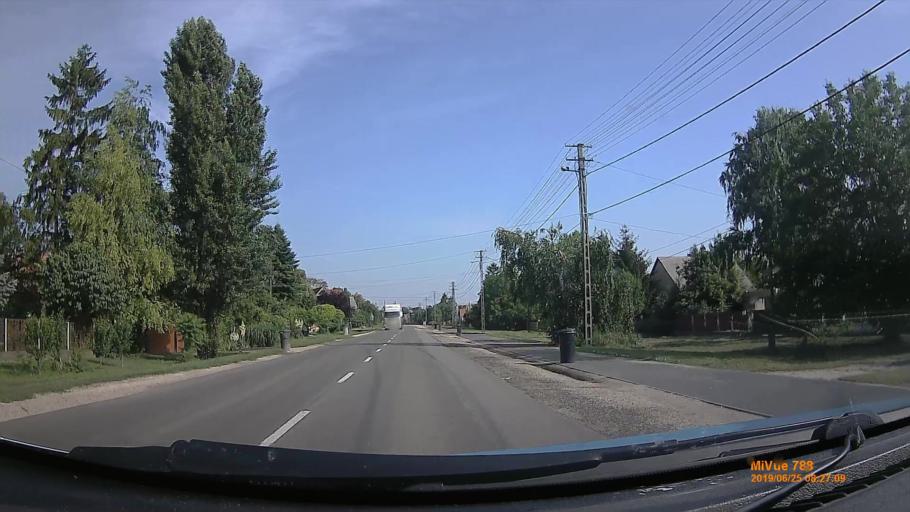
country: HU
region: Fejer
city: Szabadbattyan
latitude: 47.1111
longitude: 18.3815
